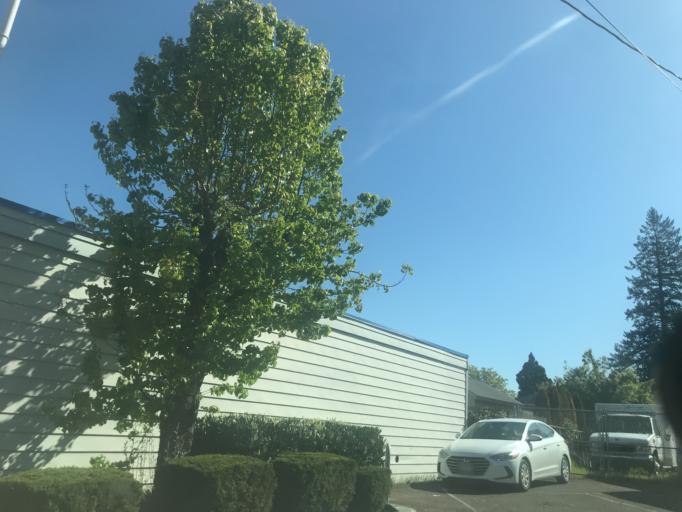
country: US
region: Oregon
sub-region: Multnomah County
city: Lents
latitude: 45.4834
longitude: -122.5892
